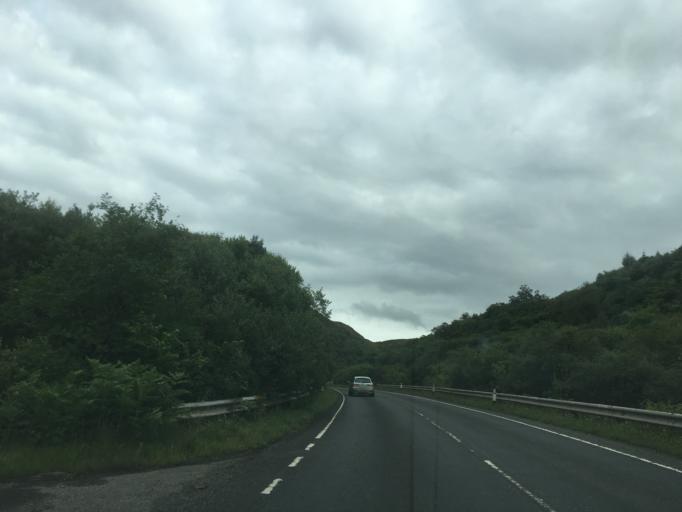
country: GB
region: Scotland
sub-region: Argyll and Bute
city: Oban
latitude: 56.3098
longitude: -5.4690
